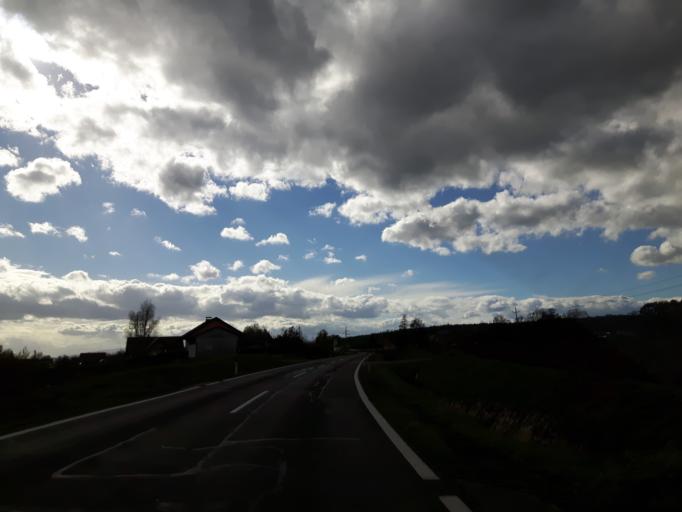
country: AT
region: Styria
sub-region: Politischer Bezirk Leibnitz
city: Breitenfeld am Tannenriegel
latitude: 46.8480
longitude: 15.6427
